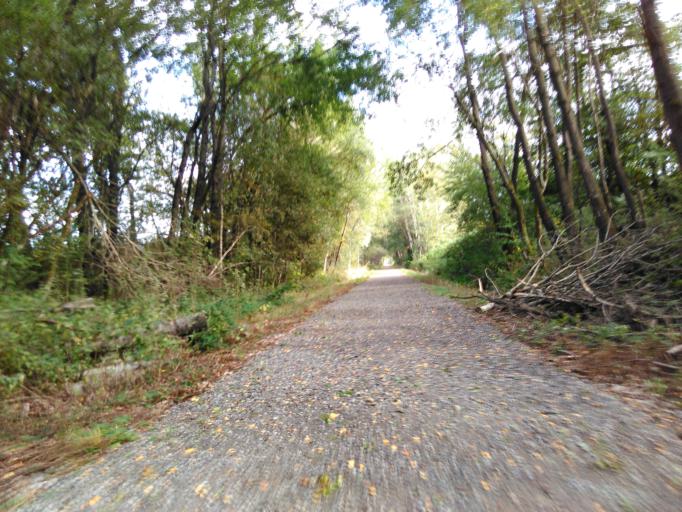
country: BE
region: Wallonia
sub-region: Province du Luxembourg
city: Vaux-sur-Sure
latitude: 49.9207
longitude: 5.5069
